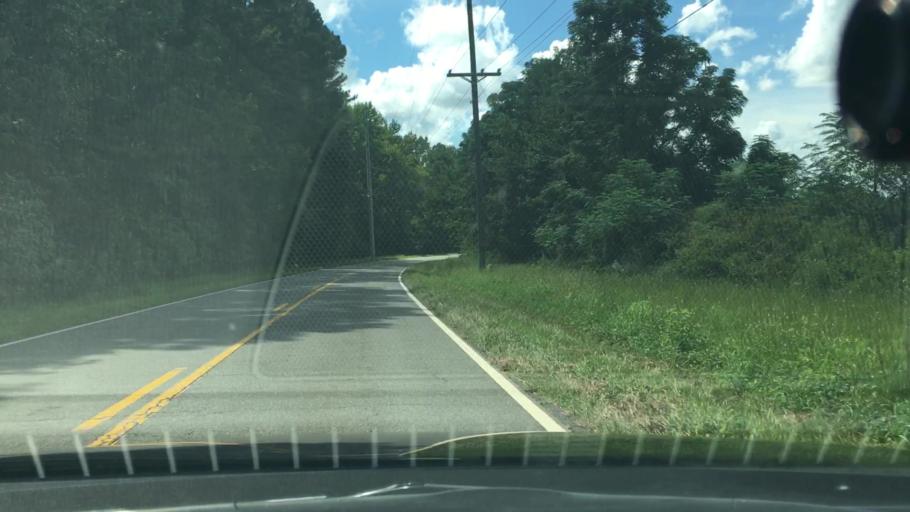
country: US
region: Georgia
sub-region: Putnam County
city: Jefferson
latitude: 33.3670
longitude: -83.2834
